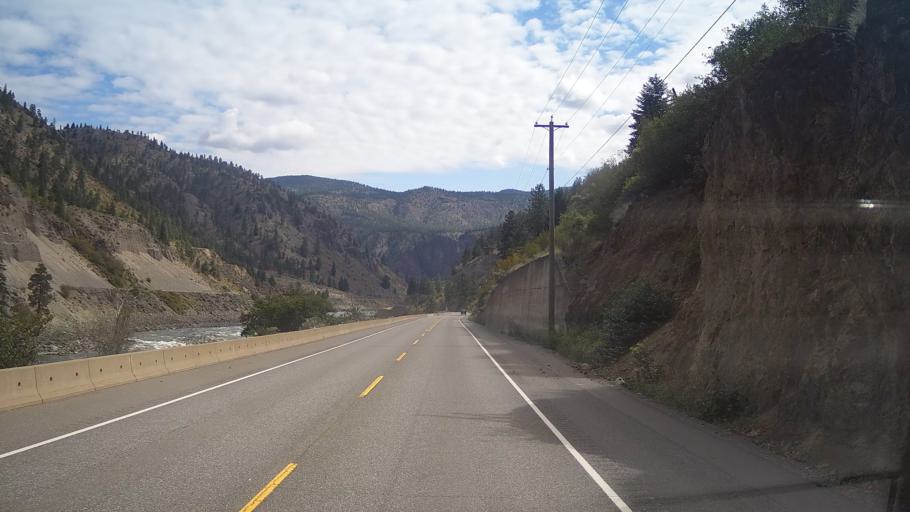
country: CA
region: British Columbia
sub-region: Thompson-Nicola Regional District
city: Ashcroft
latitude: 50.2597
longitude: -121.4275
